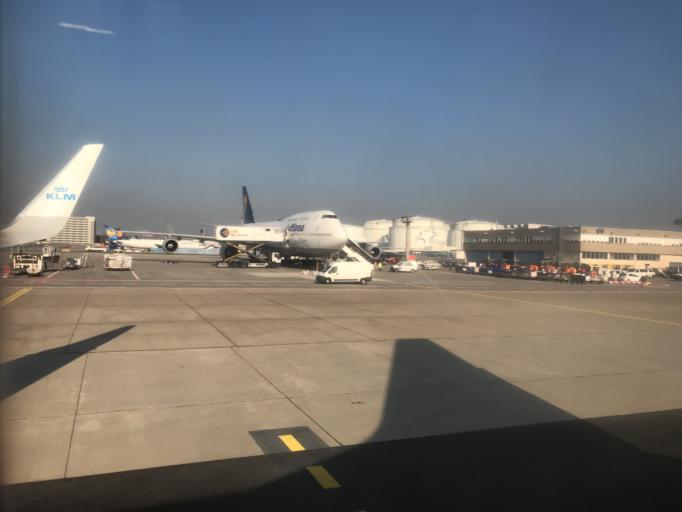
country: DE
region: Hesse
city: Kelsterbach
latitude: 50.0385
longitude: 8.5514
